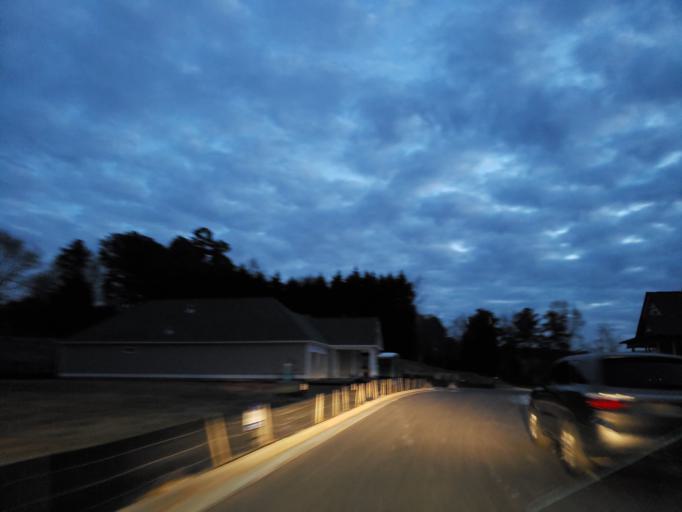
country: US
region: Georgia
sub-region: Cobb County
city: Kennesaw
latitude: 33.9996
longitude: -84.6461
